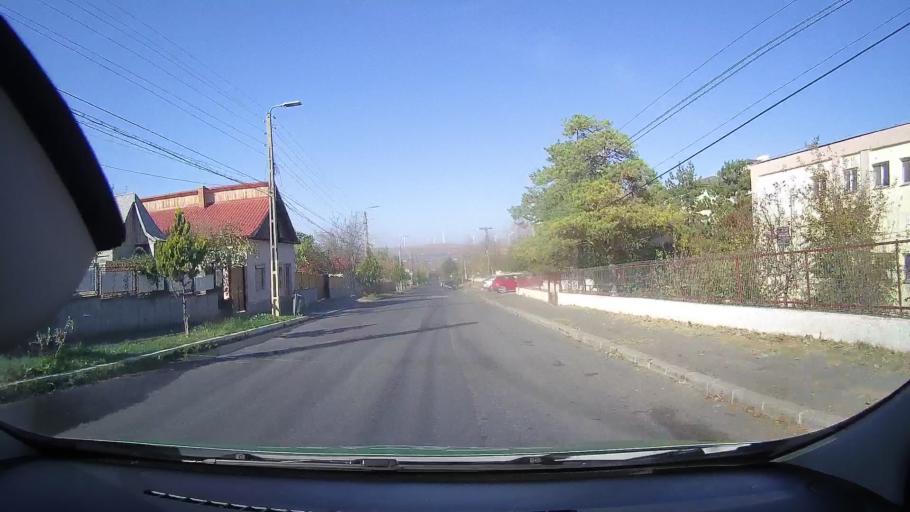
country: RO
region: Tulcea
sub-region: Oras Babadag
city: Babadag
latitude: 44.8873
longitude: 28.7333
